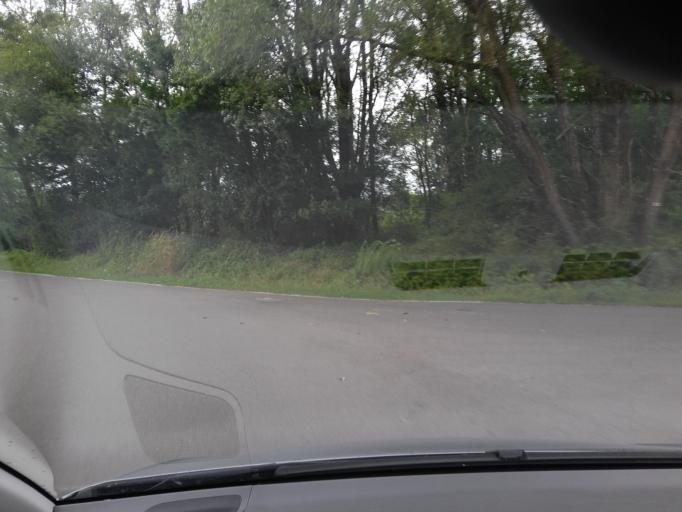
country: BE
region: Wallonia
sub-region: Province du Luxembourg
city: Arlon
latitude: 49.7214
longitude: 5.8171
